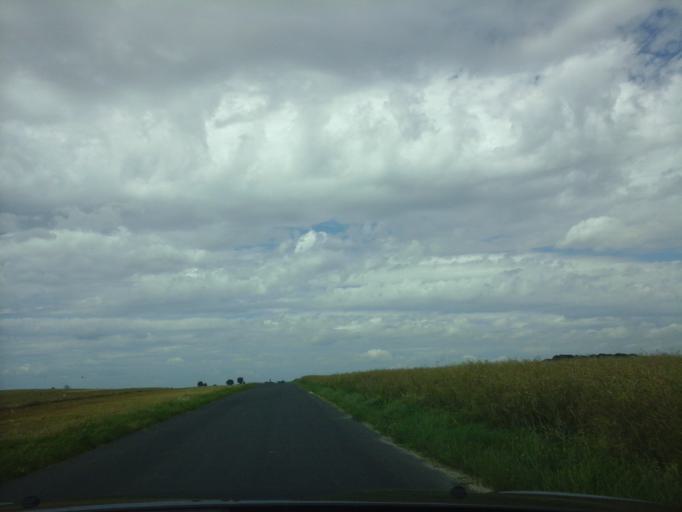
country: PL
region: West Pomeranian Voivodeship
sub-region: Powiat choszczenski
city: Recz
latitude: 53.2775
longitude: 15.4932
